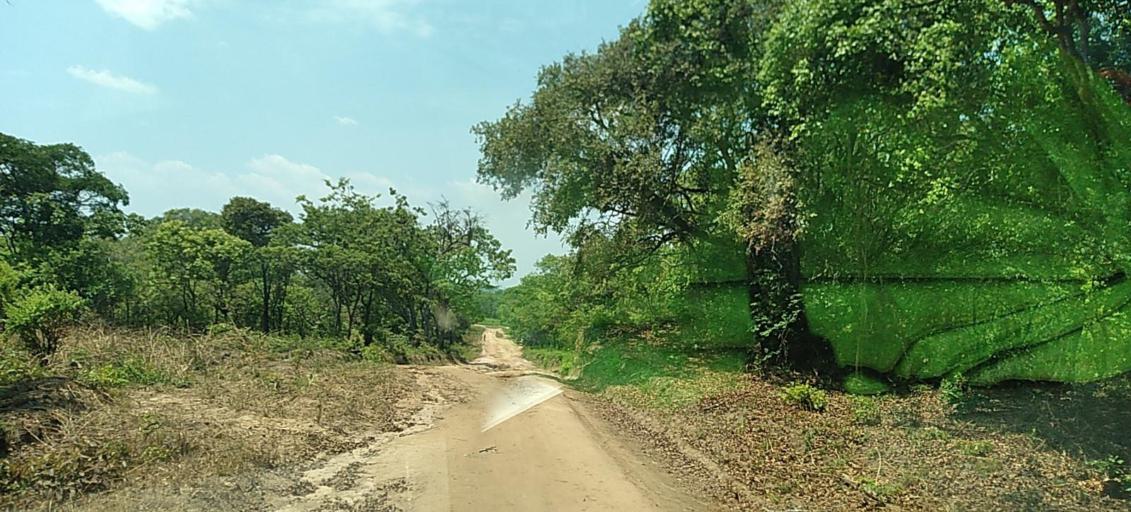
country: CD
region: Katanga
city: Kolwezi
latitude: -11.3156
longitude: 25.2345
